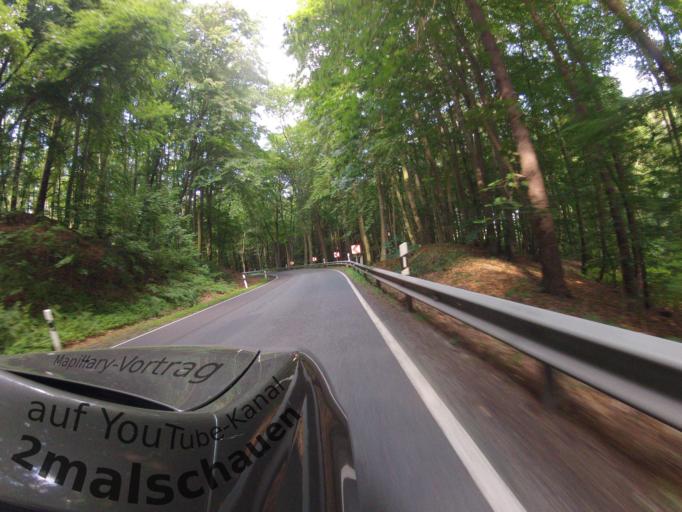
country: DE
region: Mecklenburg-Vorpommern
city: Seebad Heringsdorf
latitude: 53.9211
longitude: 14.1693
